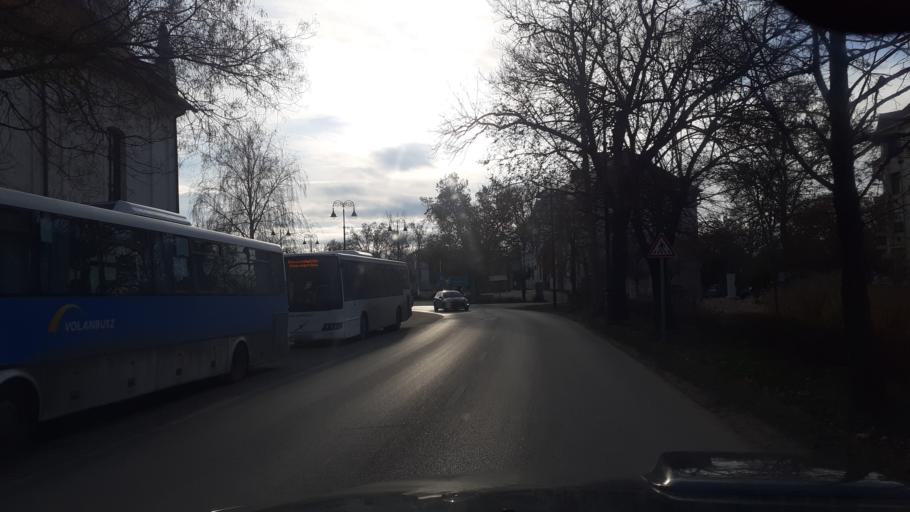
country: HU
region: Bacs-Kiskun
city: Kunszentmiklos
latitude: 47.0274
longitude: 19.1232
